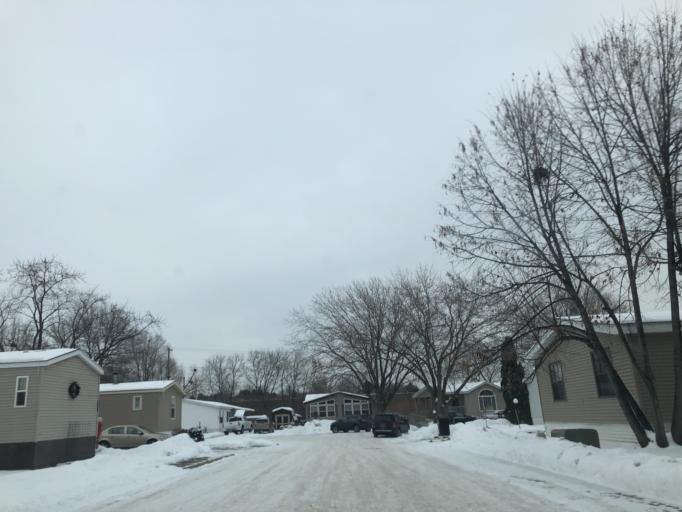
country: US
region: Minnesota
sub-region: Ramsey County
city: New Brighton
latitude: 45.0798
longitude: -93.1803
